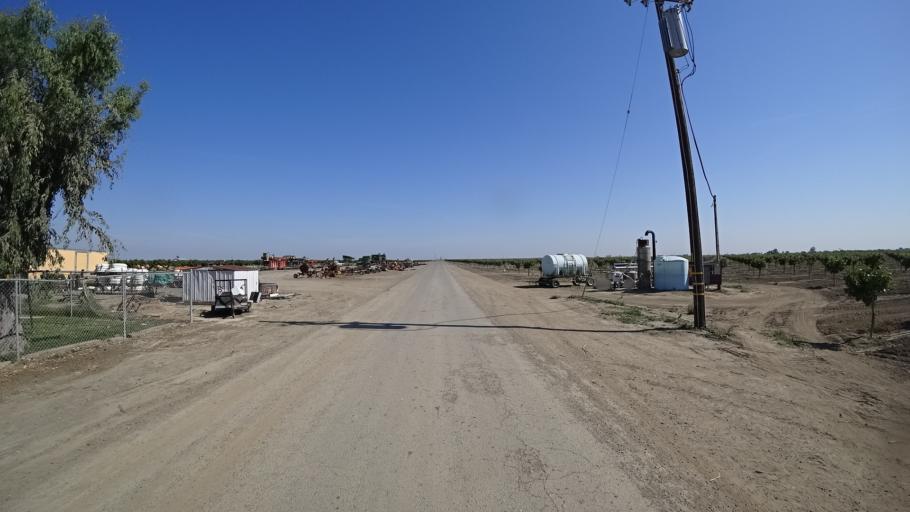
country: US
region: California
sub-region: Fresno County
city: Riverdale
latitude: 36.3800
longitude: -119.9412
